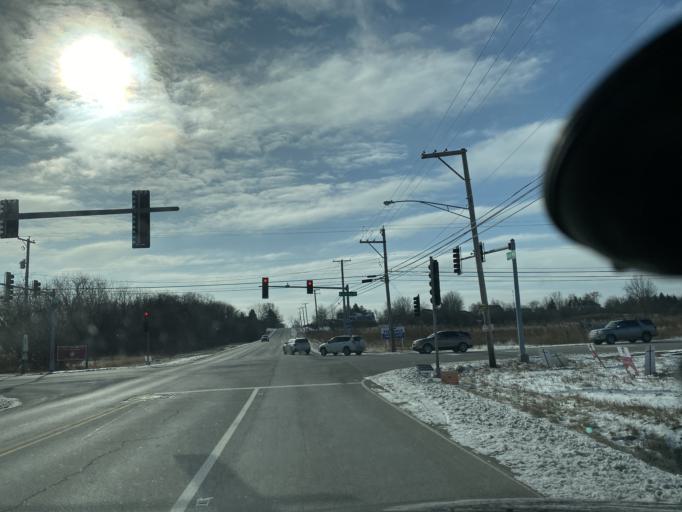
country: US
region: Illinois
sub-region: Will County
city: Goodings Grove
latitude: 41.6657
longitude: -87.9321
